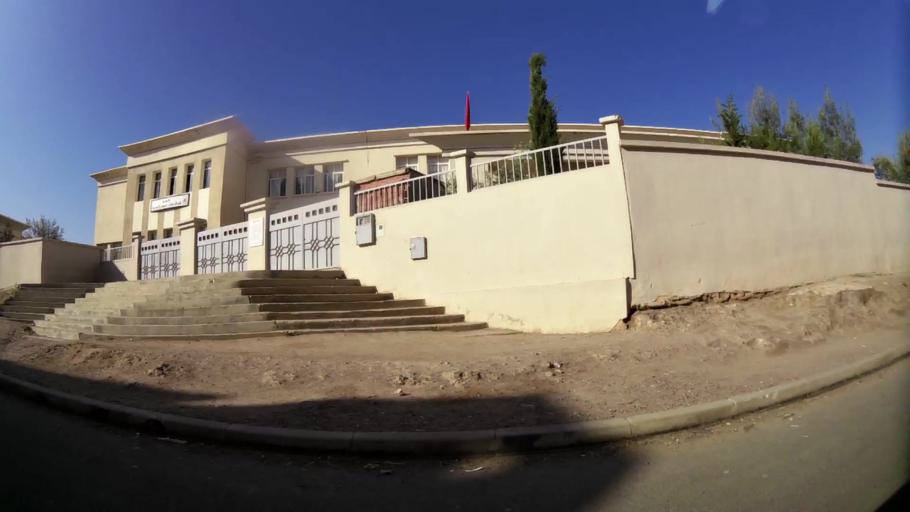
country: MA
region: Oriental
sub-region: Oujda-Angad
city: Oujda
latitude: 34.6803
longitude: -1.9449
